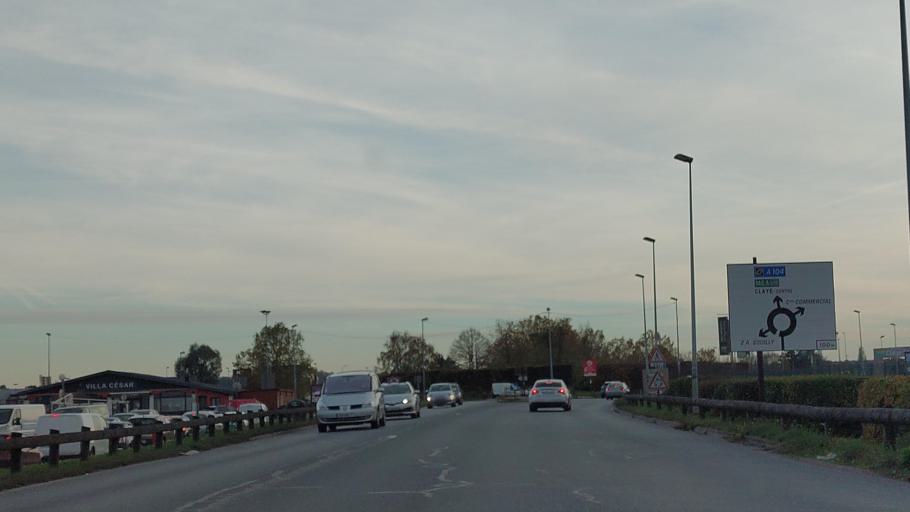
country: FR
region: Ile-de-France
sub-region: Departement de Seine-et-Marne
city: Claye-Souilly
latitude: 48.9483
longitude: 2.6673
